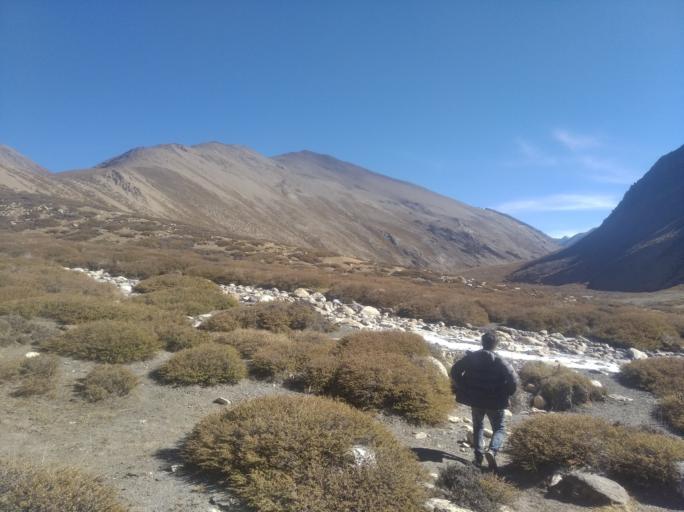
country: NP
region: Western Region
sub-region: Dhawalagiri Zone
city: Jomsom
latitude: 29.1835
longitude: 83.3161
